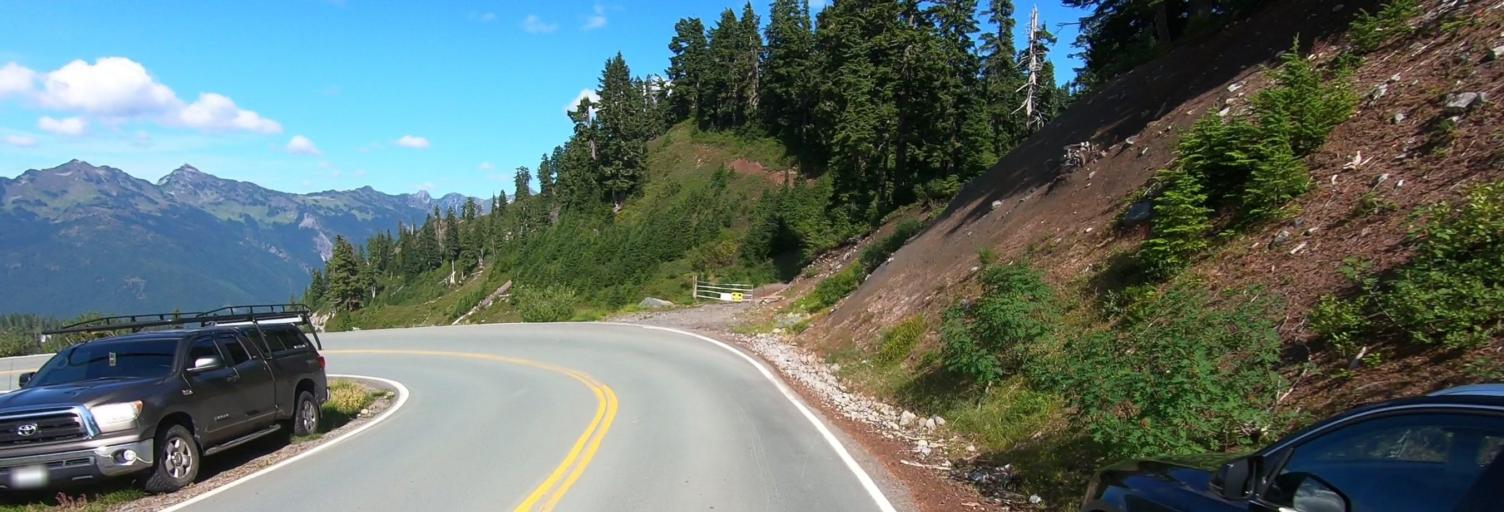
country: CA
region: British Columbia
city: Agassiz
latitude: 48.8503
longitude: -121.6829
